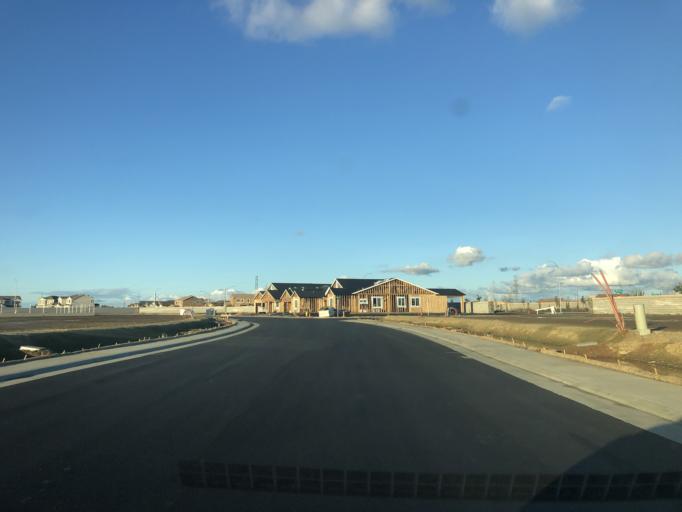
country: US
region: California
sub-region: Sacramento County
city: Antelope
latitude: 38.7580
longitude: -121.3643
